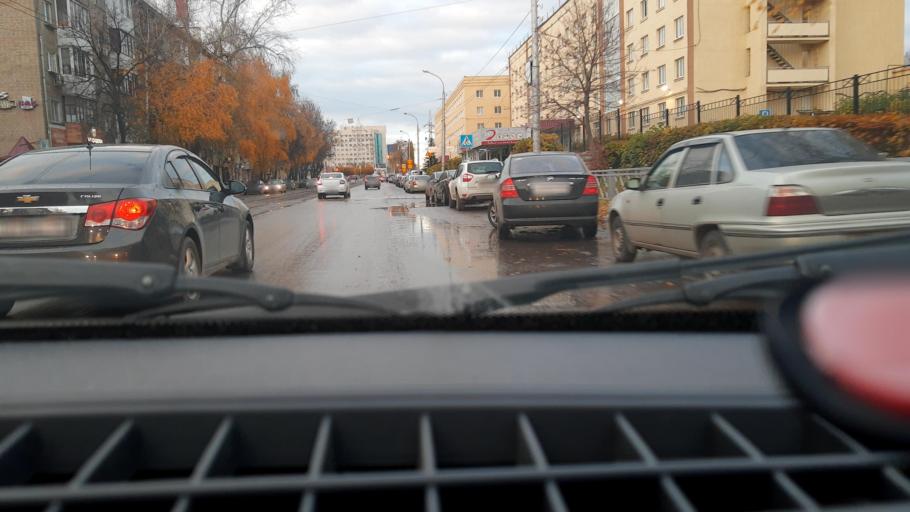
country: RU
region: Bashkortostan
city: Ufa
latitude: 54.7353
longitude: 55.9713
